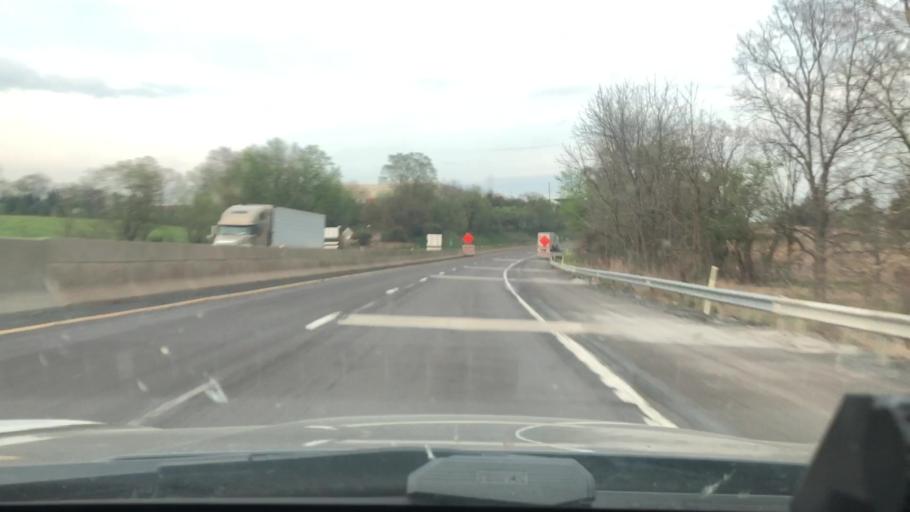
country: US
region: Pennsylvania
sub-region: Berks County
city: Kutztown
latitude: 40.5810
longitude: -75.7273
